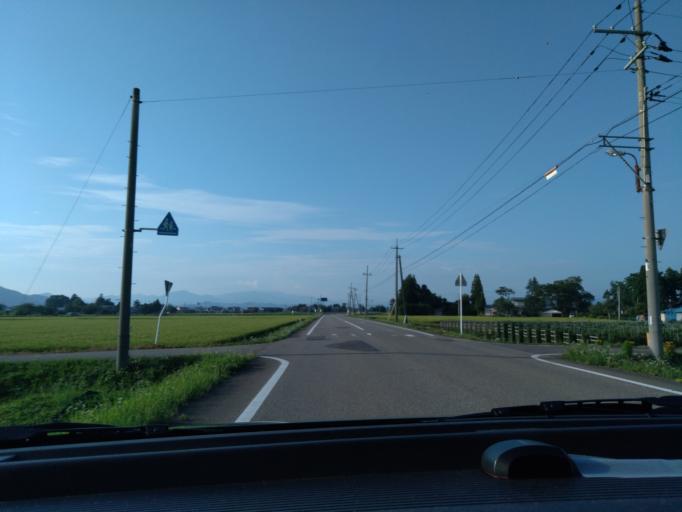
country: JP
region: Akita
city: Kakunodatemachi
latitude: 39.5141
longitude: 140.5587
